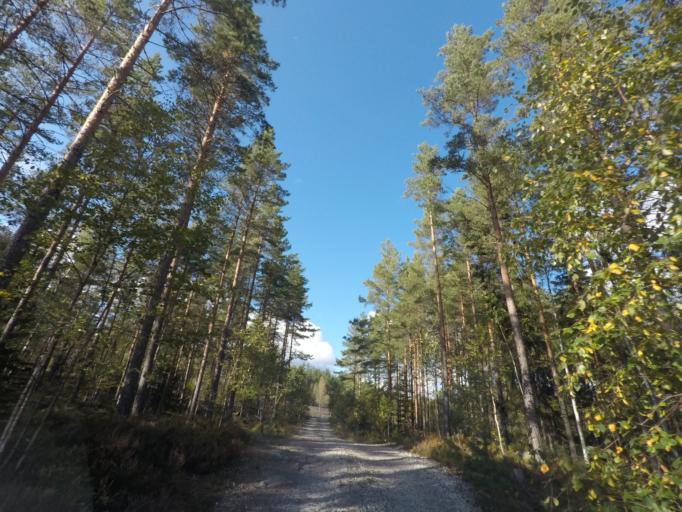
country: SE
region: Vaestmanland
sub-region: Skinnskattebergs Kommun
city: Skinnskatteberg
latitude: 59.8316
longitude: 15.5494
